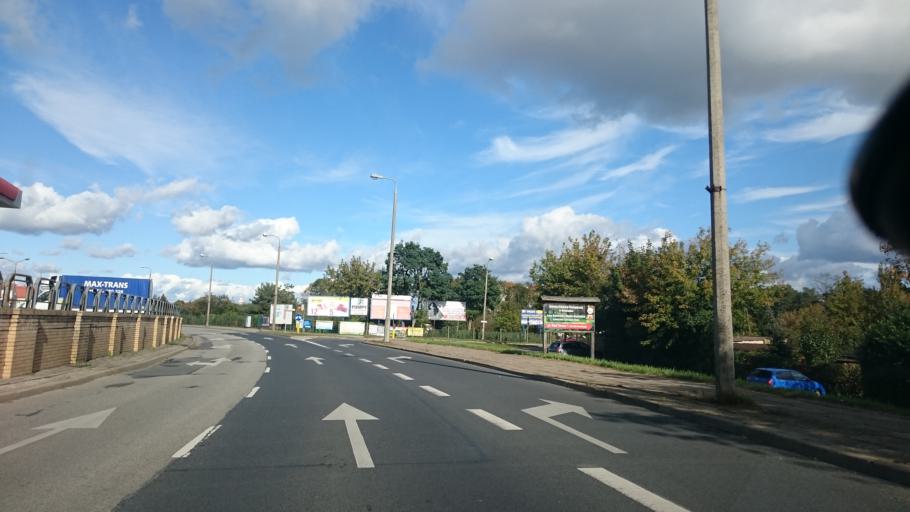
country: PL
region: Kujawsko-Pomorskie
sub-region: Grudziadz
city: Grudziadz
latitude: 53.4635
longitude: 18.7419
